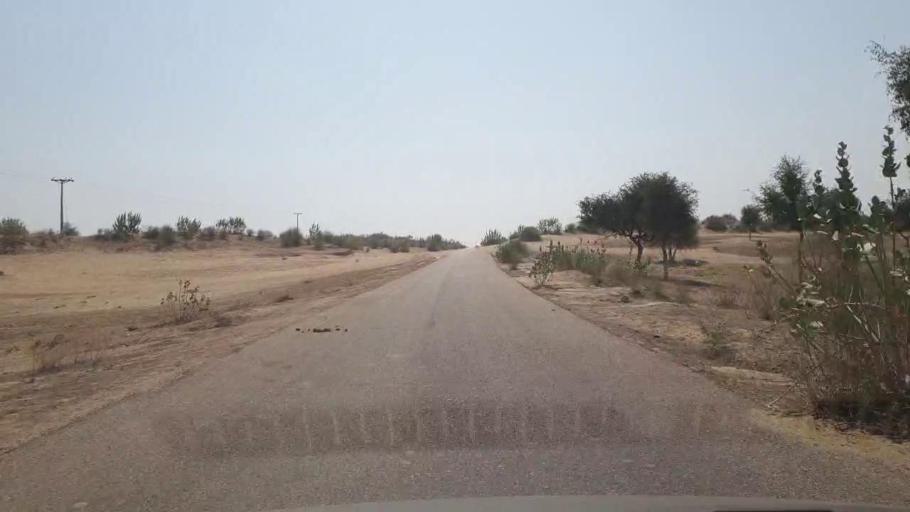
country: PK
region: Sindh
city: Chor
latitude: 25.6397
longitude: 70.1724
